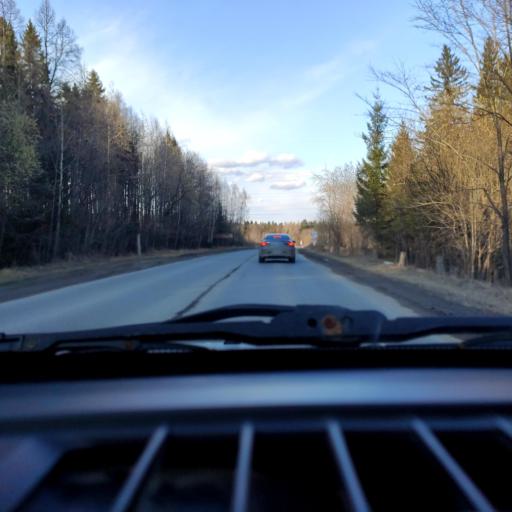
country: RU
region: Perm
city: Ferma
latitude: 57.9627
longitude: 56.3484
